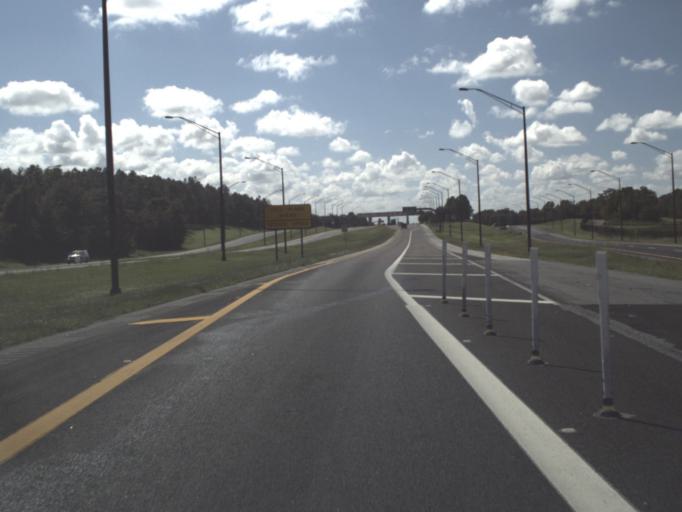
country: US
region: Florida
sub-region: Citrus County
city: Sugarmill Woods
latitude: 28.6641
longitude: -82.4936
